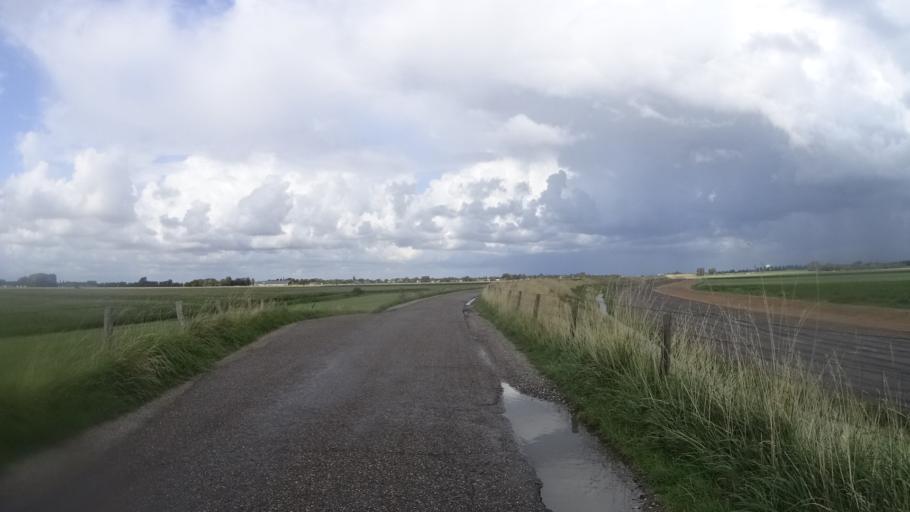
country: NL
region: North Holland
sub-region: Gemeente Schagen
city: Schagen
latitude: 52.7853
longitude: 4.7481
